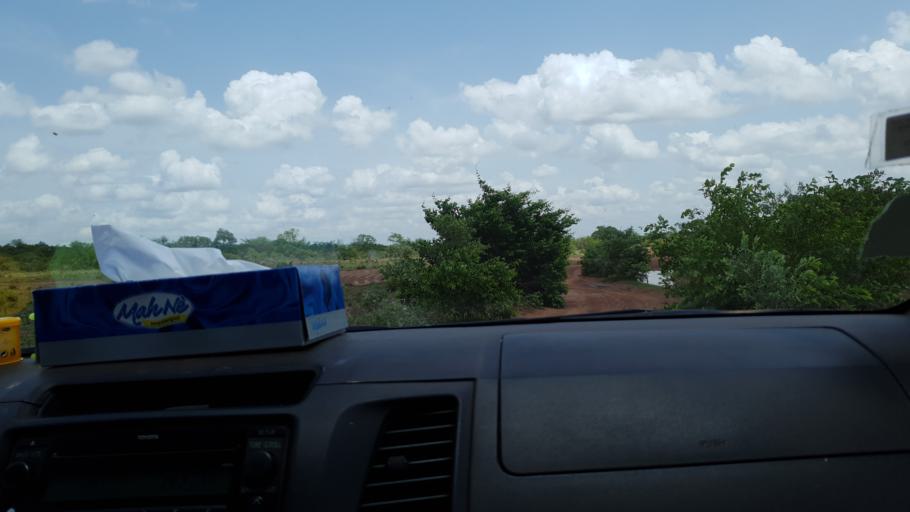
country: ML
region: Koulikoro
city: Banamba
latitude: 13.3781
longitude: -7.2104
